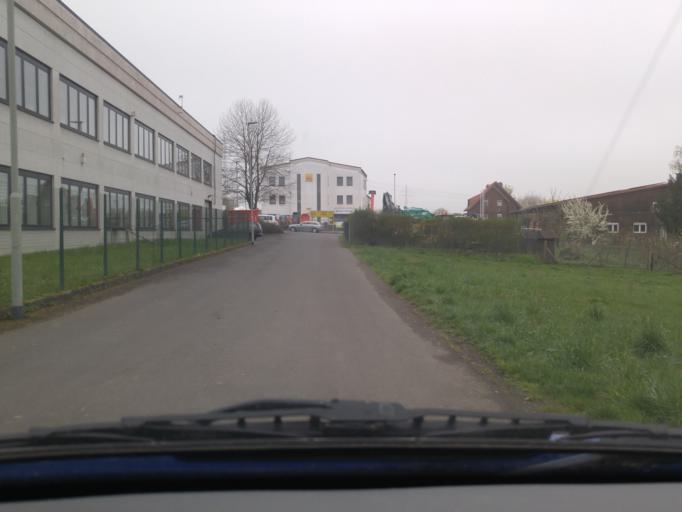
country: DE
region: Hesse
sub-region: Regierungsbezirk Darmstadt
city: Karben
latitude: 50.2811
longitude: 8.7670
